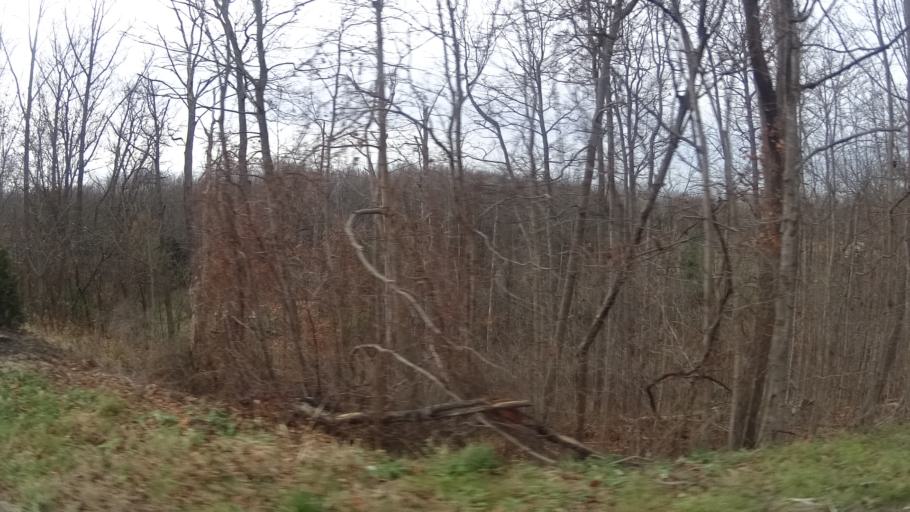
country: US
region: Ohio
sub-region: Cuyahoga County
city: Strongsville
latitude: 41.2928
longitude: -81.9114
